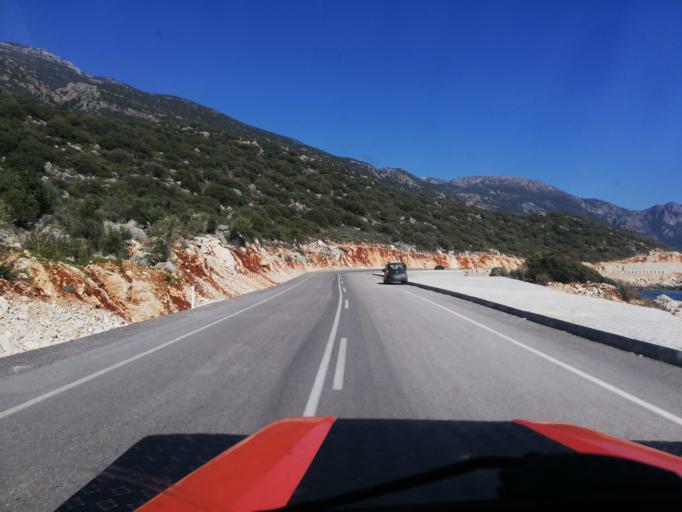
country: TR
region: Antalya
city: Kas
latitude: 36.2027
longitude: 29.5910
